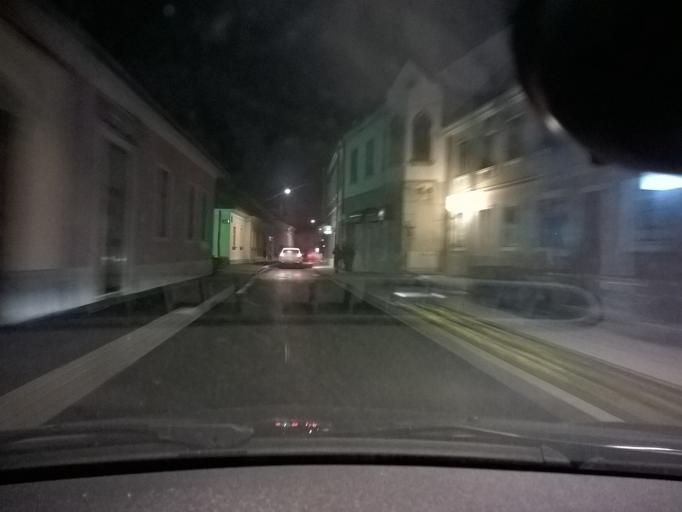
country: HR
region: Krapinsko-Zagorska
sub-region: Grad Krapina
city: Krapina
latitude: 46.1632
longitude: 15.8719
